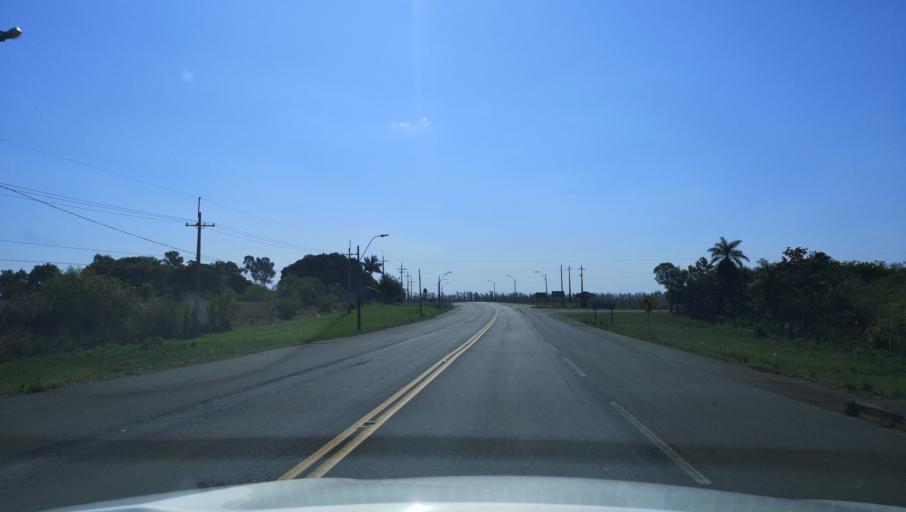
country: PY
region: Misiones
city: San Patricio
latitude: -27.0009
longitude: -56.7373
